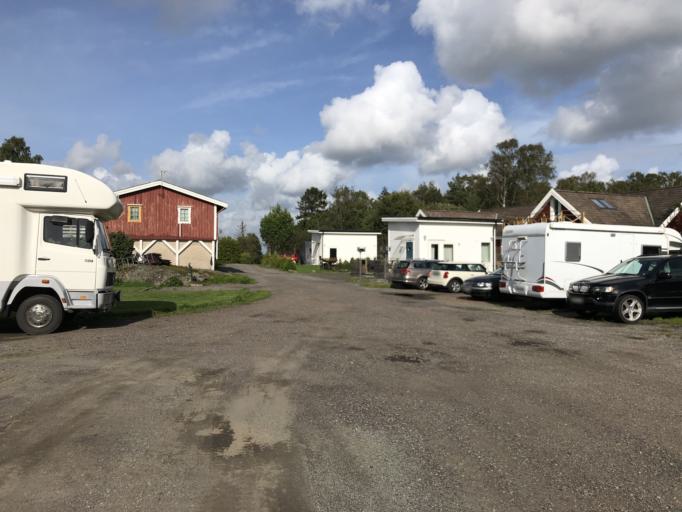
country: SE
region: Vaestra Goetaland
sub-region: Goteborg
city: Majorna
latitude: 57.7481
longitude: 11.8602
